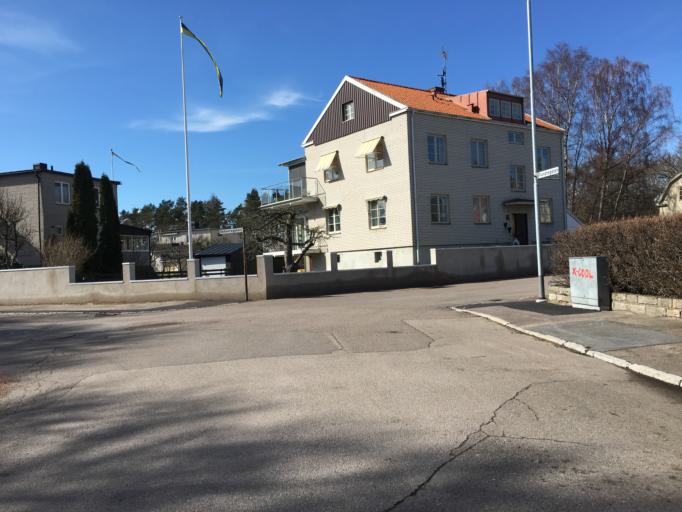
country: SE
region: Kalmar
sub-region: Kalmar Kommun
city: Kalmar
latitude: 56.6526
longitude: 16.3296
